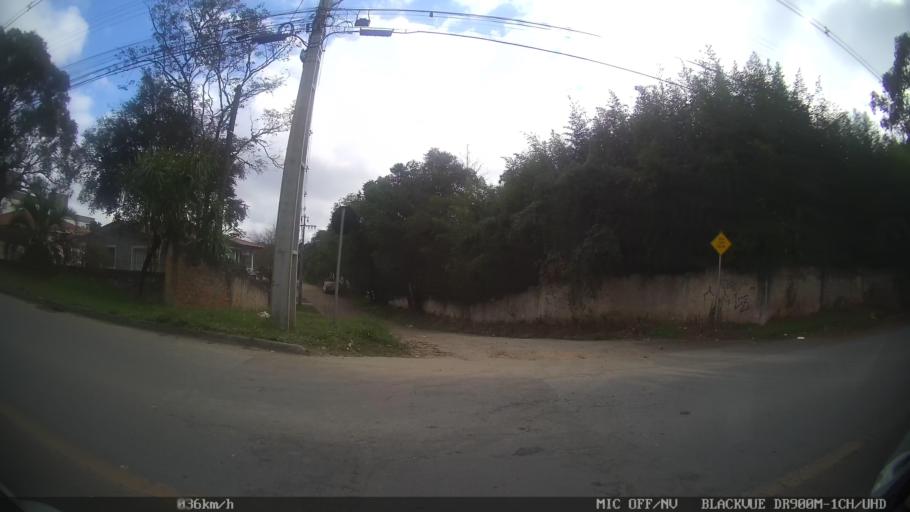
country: BR
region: Parana
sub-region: Colombo
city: Colombo
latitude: -25.3585
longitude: -49.2417
